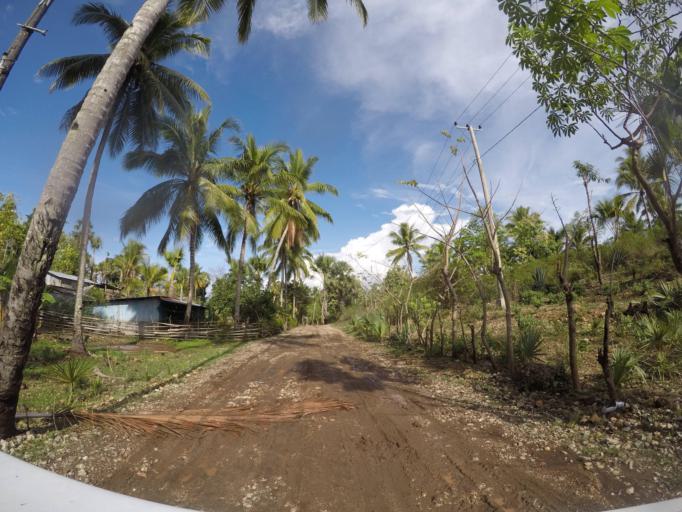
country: TL
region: Baucau
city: Baucau
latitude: -8.5013
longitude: 126.4607
